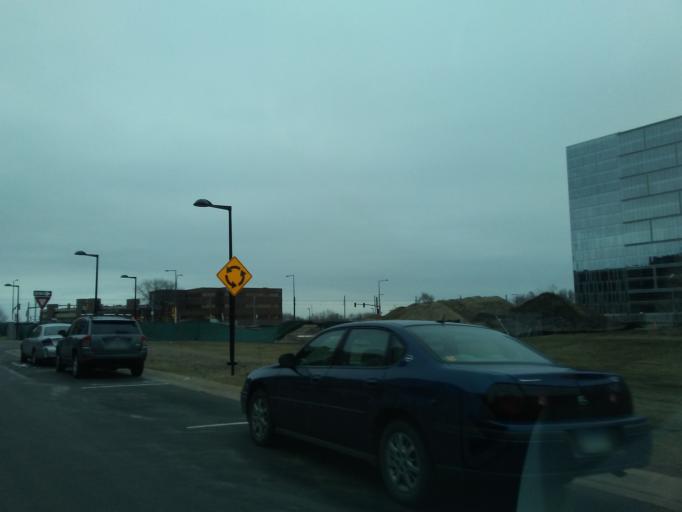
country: US
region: Minnesota
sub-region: Hennepin County
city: Richfield
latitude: 44.8575
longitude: -93.2251
